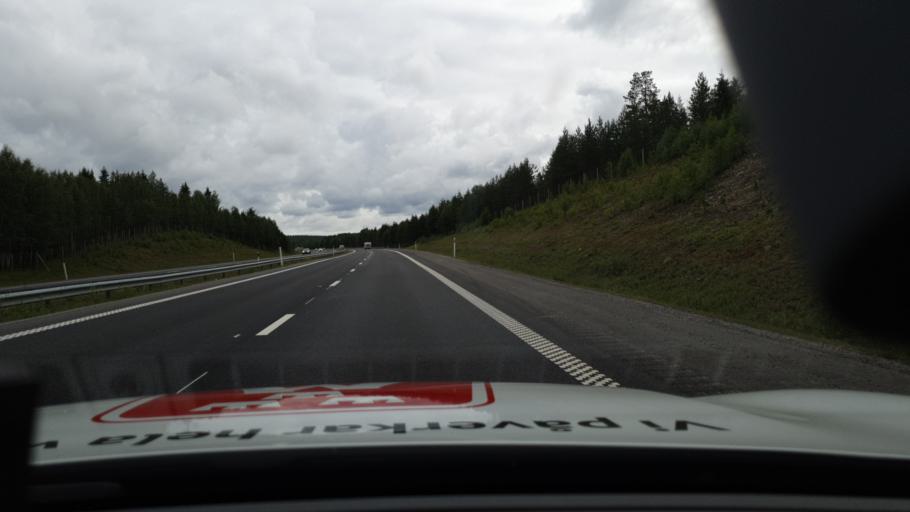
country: SE
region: Norrbotten
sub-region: Pitea Kommun
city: Norrfjarden
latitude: 65.3641
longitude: 21.4297
